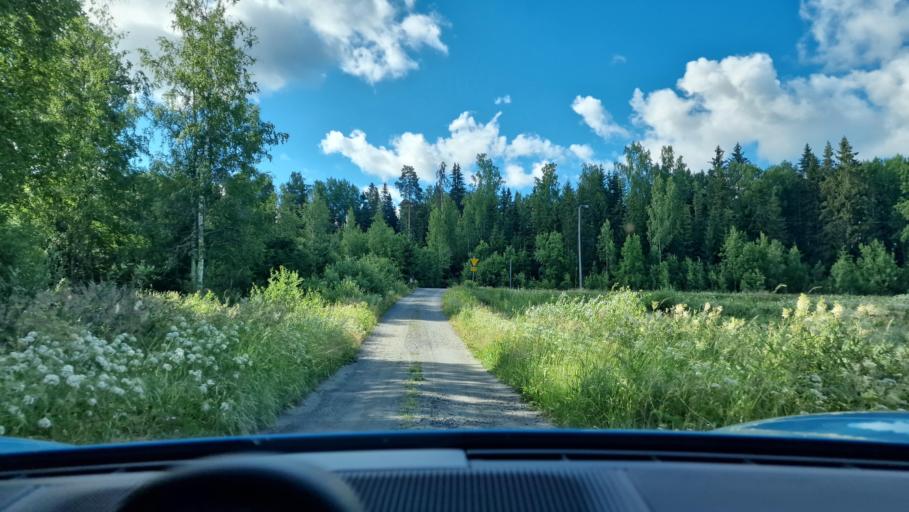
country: FI
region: Pirkanmaa
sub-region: Etelae-Pirkanmaa
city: Valkeakoski
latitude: 61.2568
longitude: 24.1527
